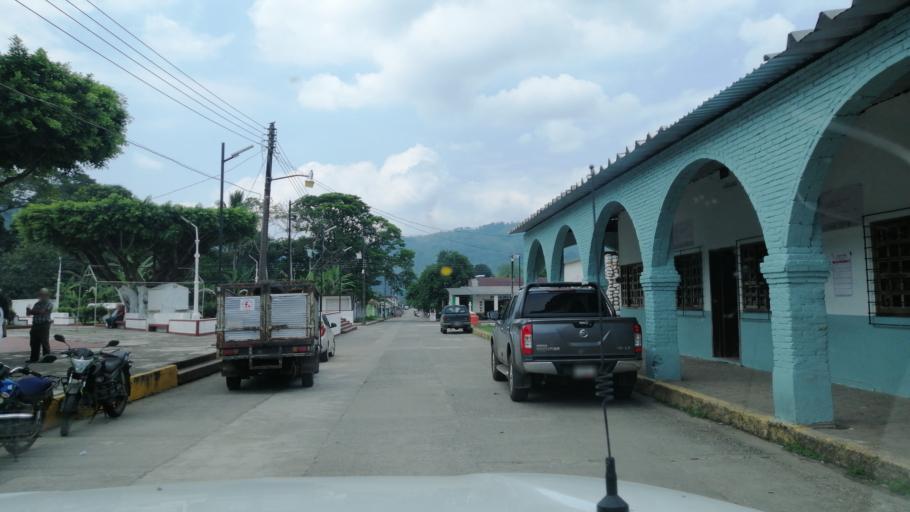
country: MX
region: Chiapas
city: Ostuacan
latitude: 17.4055
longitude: -93.3366
